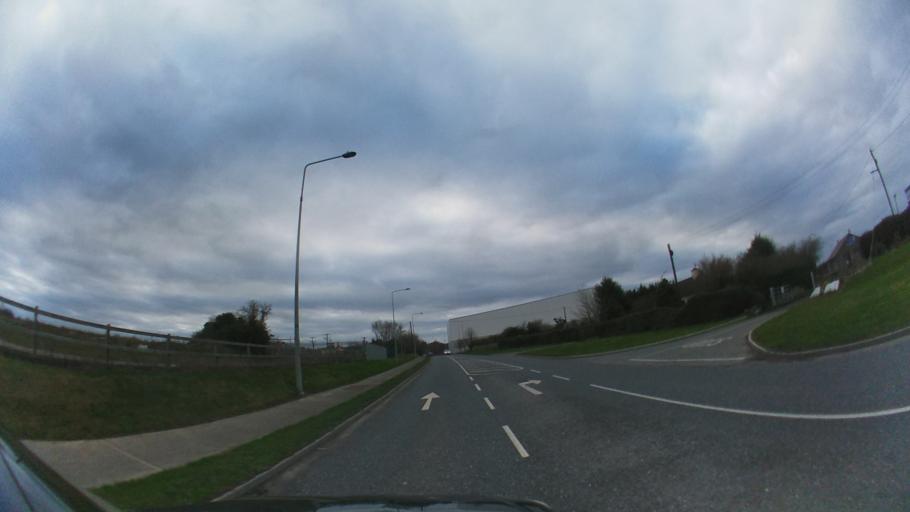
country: IE
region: Leinster
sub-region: Lu
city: Drogheda
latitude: 53.7036
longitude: -6.3578
